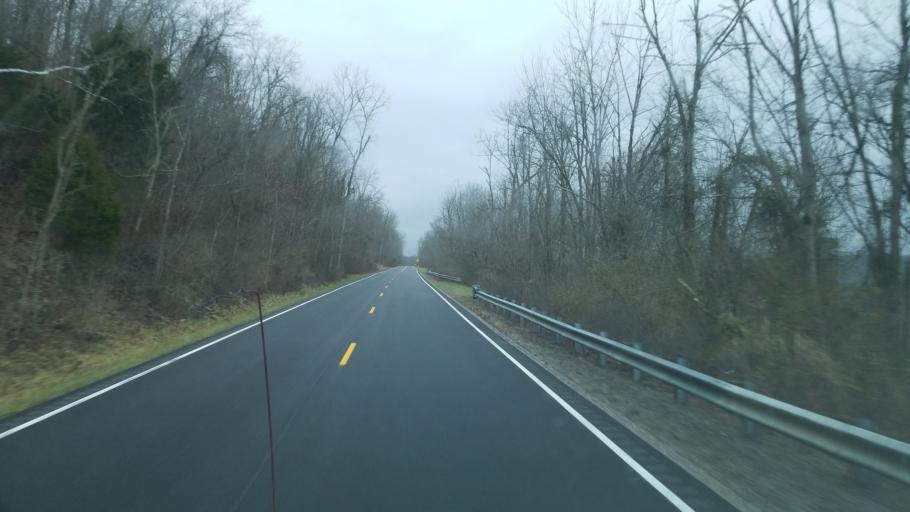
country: US
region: Kentucky
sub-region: Bracken County
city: Augusta
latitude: 38.7693
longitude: -83.9296
